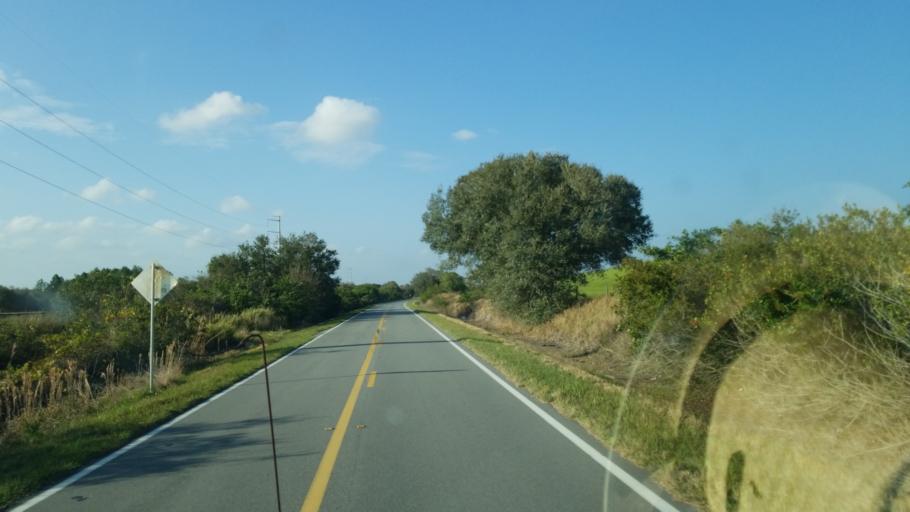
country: US
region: Florida
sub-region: Polk County
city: Mulberry
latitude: 27.7682
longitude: -81.9726
